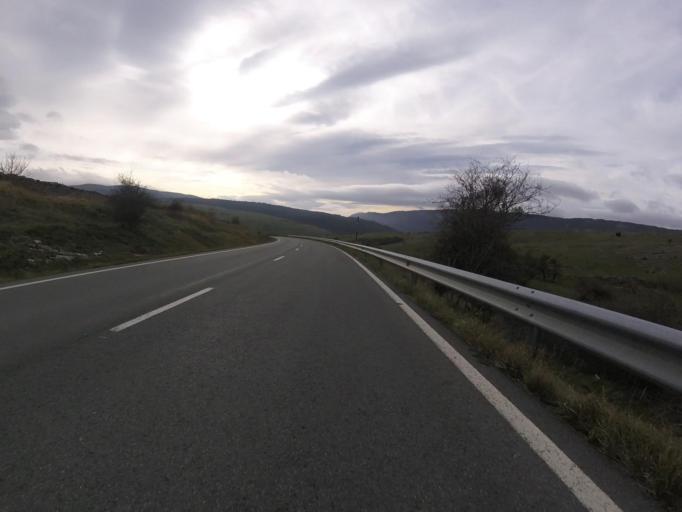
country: ES
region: Navarre
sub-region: Provincia de Navarra
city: Arbizu
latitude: 42.8503
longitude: -2.0166
